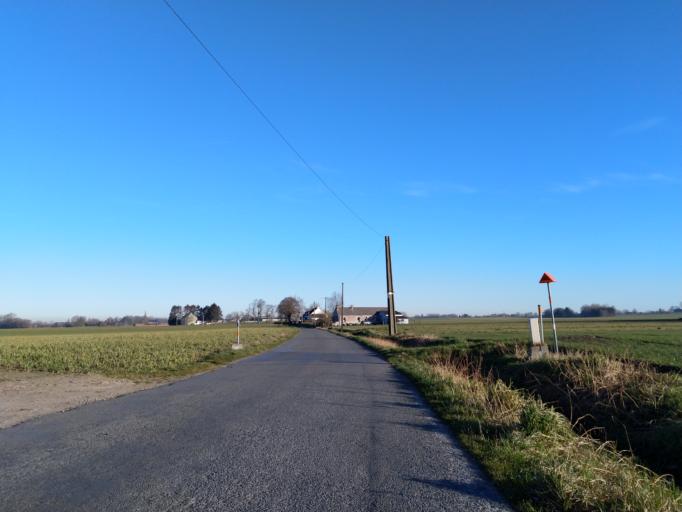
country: BE
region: Wallonia
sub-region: Province du Hainaut
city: Jurbise
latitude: 50.5184
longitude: 3.9515
